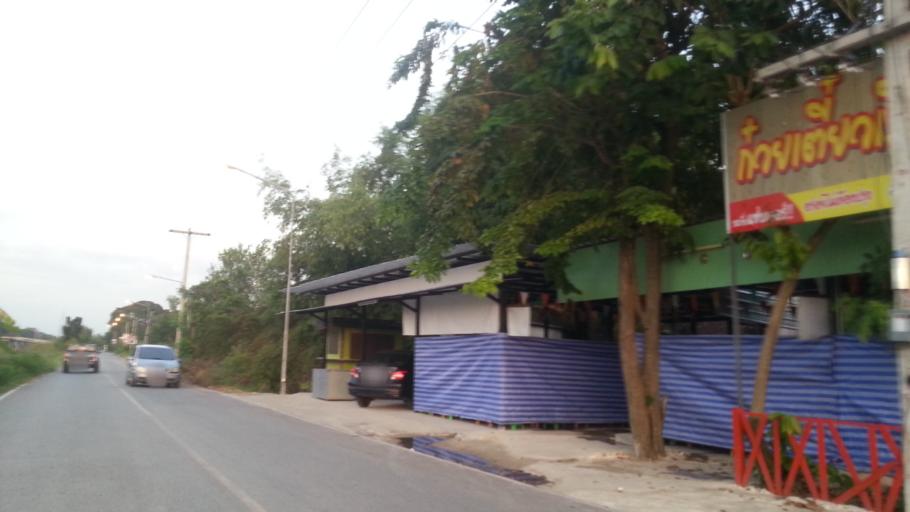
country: TH
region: Pathum Thani
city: Ban Rangsit
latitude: 14.0409
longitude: 100.7921
